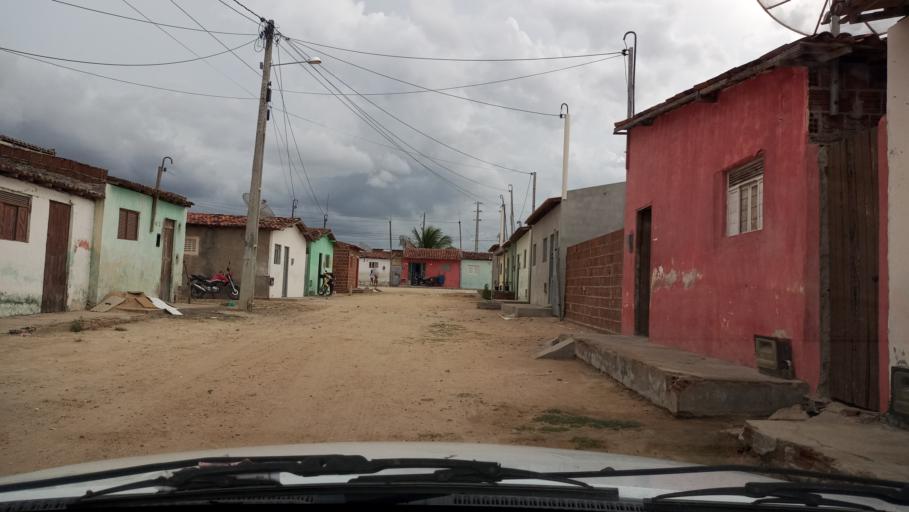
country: BR
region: Rio Grande do Norte
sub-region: Tangara
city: Tangara
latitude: -6.1909
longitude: -35.8019
